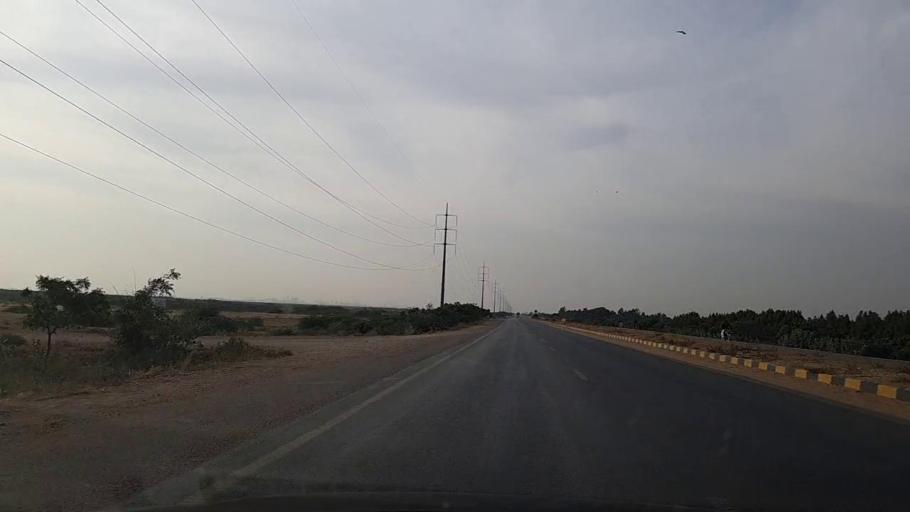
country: PK
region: Sindh
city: Gharo
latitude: 24.8218
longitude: 67.4814
